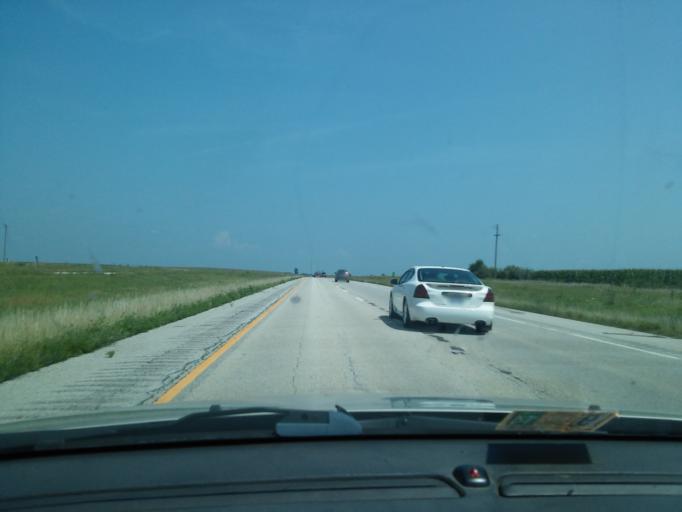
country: US
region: Illinois
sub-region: Morgan County
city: Jacksonville
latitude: 39.7380
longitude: -90.1137
